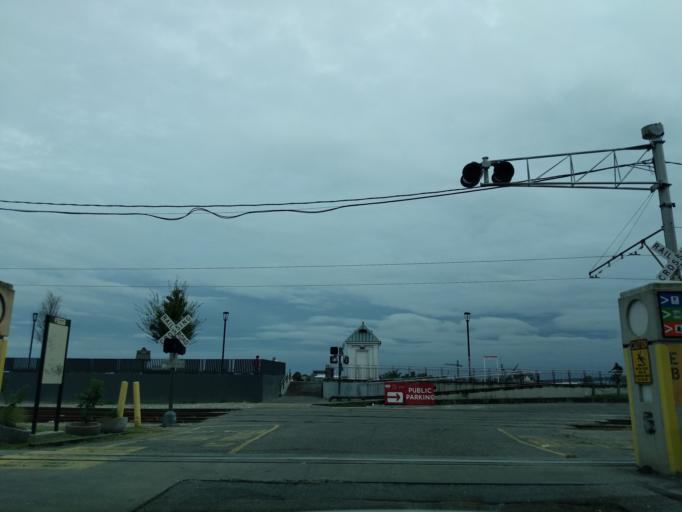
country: US
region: Louisiana
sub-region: Orleans Parish
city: New Orleans
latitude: 29.9565
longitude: -90.0624
